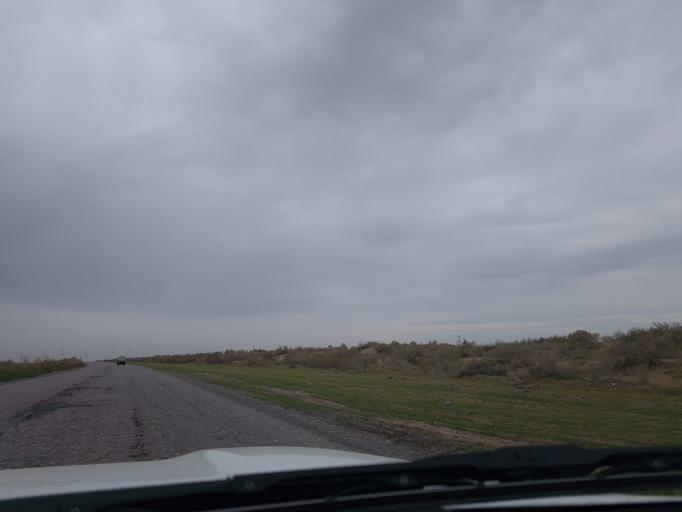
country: TM
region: Lebap
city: Turkmenabat
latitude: 38.8546
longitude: 63.4069
